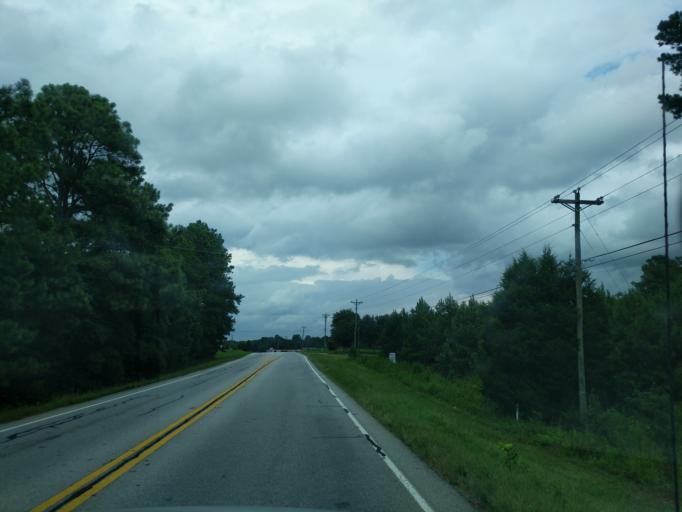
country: US
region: Georgia
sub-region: Walton County
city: Loganville
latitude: 33.8115
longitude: -83.9395
